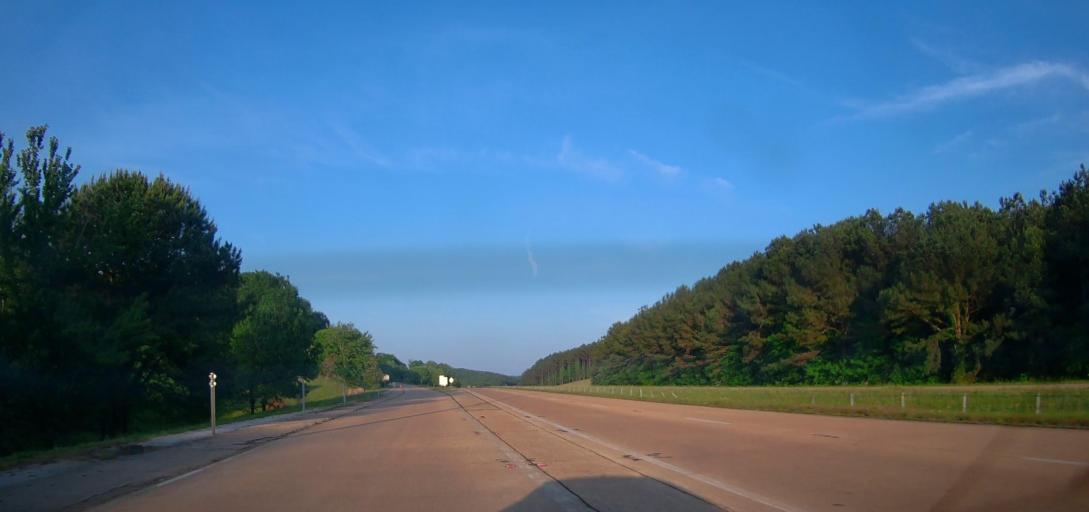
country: US
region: Mississippi
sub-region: Itawamba County
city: Fulton
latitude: 34.2207
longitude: -88.2387
